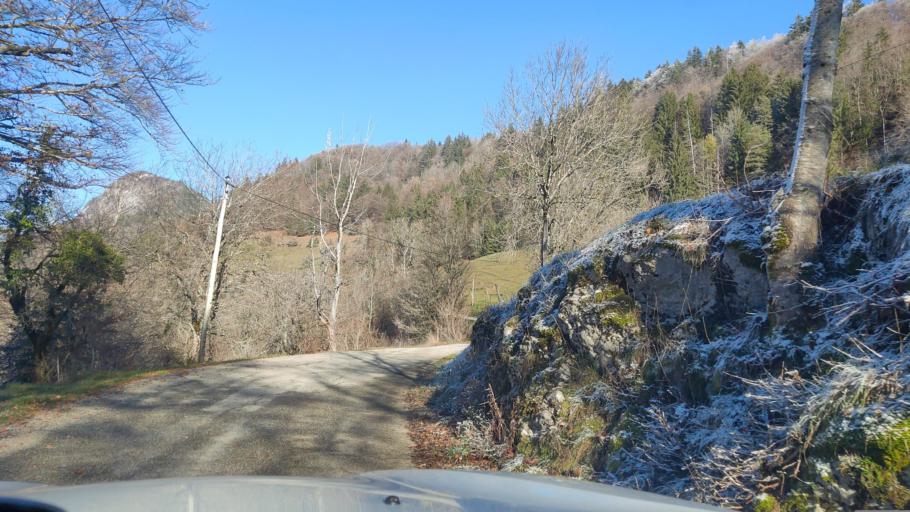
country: FR
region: Rhone-Alpes
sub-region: Departement de la Haute-Savoie
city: Doussard
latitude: 45.6856
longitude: 6.1406
